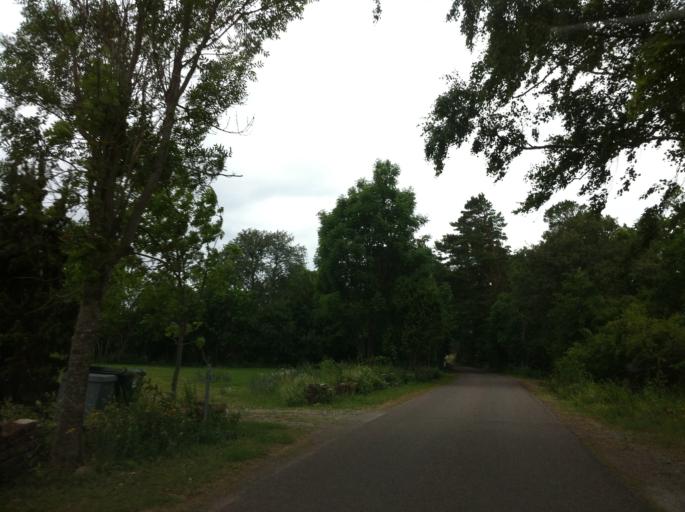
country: SE
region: Kalmar
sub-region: Oskarshamns Kommun
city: Oskarshamn
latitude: 57.3161
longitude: 16.9943
